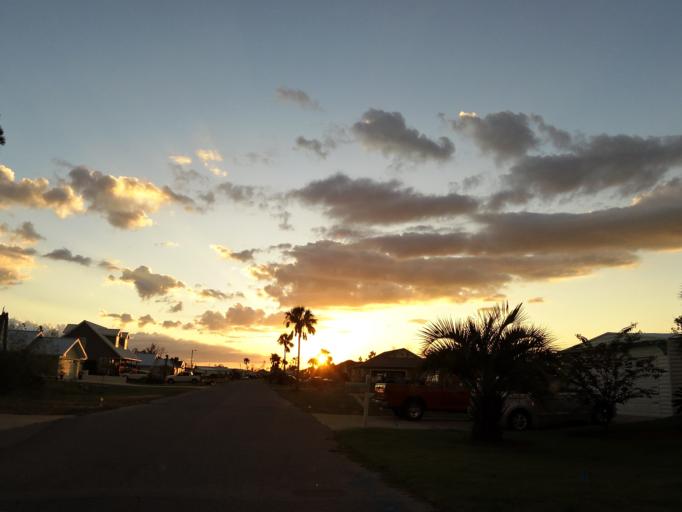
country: US
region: Florida
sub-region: Bay County
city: Mexico Beach
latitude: 29.9398
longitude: -85.3891
